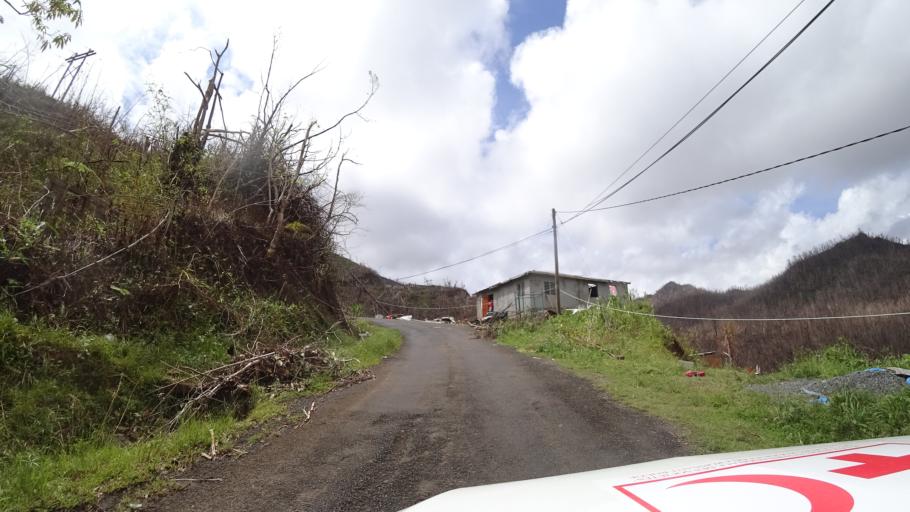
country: DM
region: Saint David
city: Rosalie
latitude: 15.3980
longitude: -61.2587
